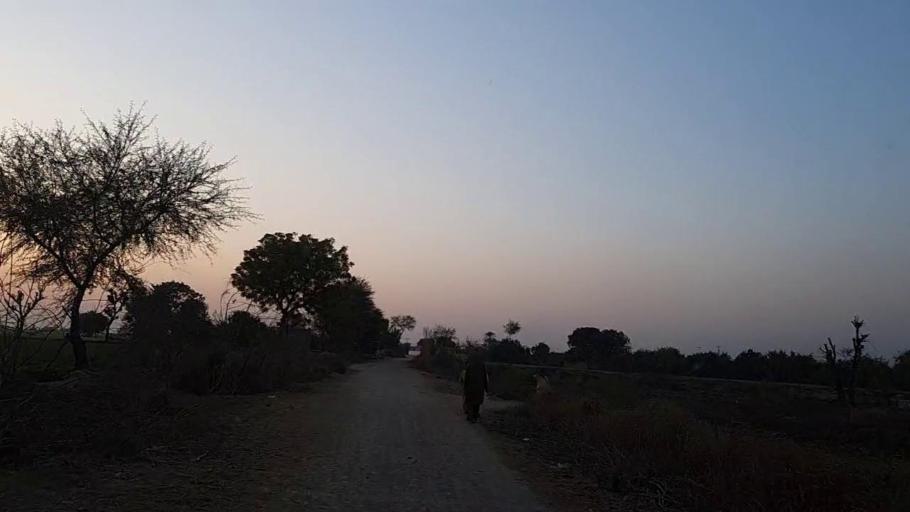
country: PK
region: Sindh
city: Hala
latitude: 25.9371
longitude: 68.4585
